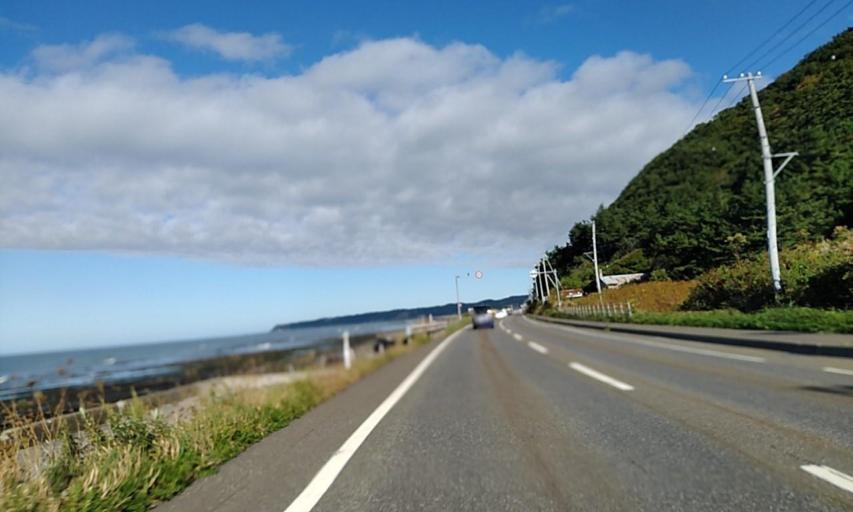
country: JP
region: Hokkaido
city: Shizunai-furukawacho
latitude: 42.2834
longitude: 142.4660
